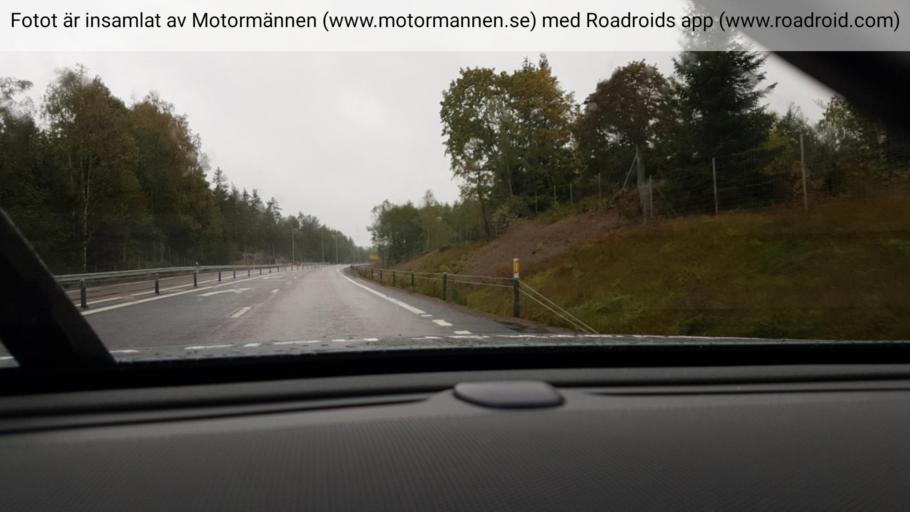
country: SE
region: Vaestra Goetaland
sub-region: Amals Kommun
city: Amal
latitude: 58.9422
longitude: 12.6003
